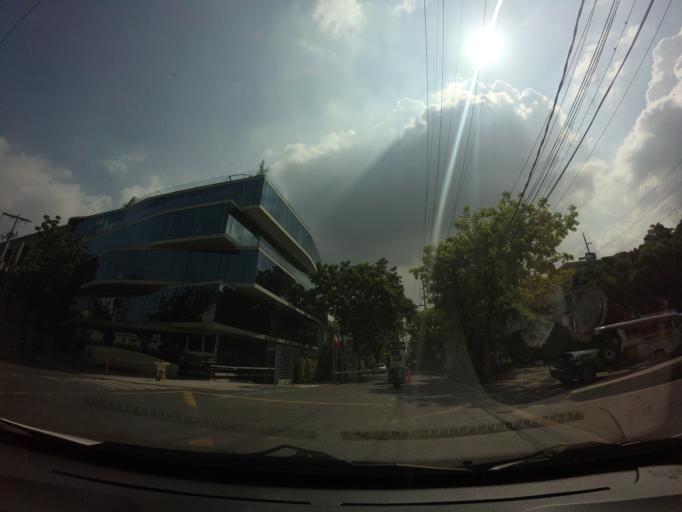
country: PH
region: Metro Manila
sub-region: Makati City
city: Makati City
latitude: 14.5559
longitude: 121.0351
